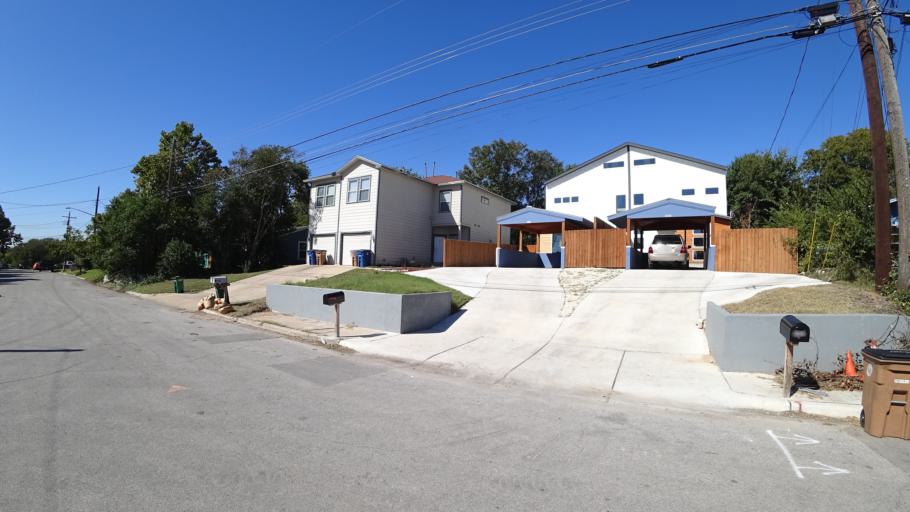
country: US
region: Texas
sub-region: Travis County
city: Austin
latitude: 30.2832
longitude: -97.6794
